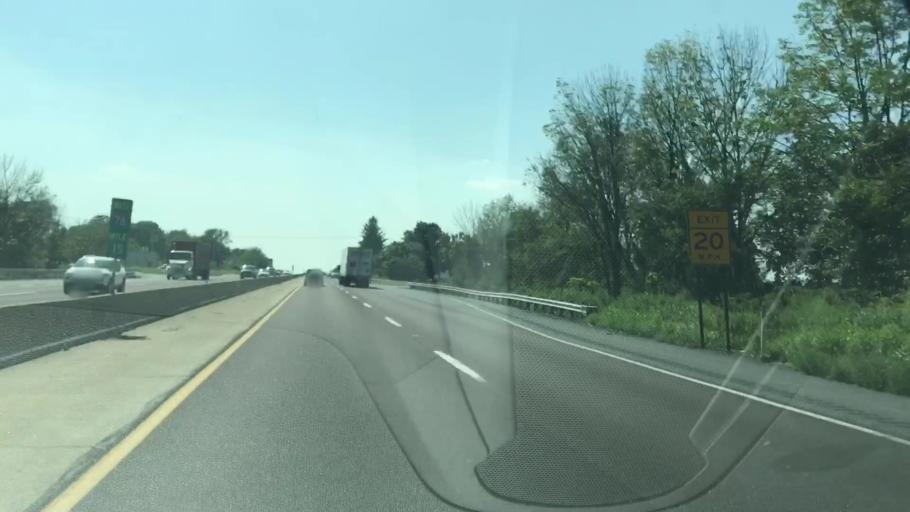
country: US
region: Pennsylvania
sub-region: Lebanon County
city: Myerstown
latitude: 40.4840
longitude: -76.2569
